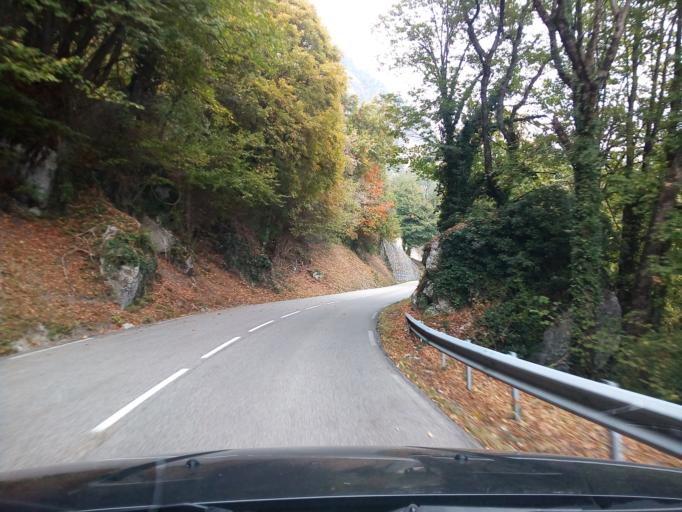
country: FR
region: Rhone-Alpes
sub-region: Departement de l'Isere
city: Bernin
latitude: 45.2754
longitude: 5.8464
